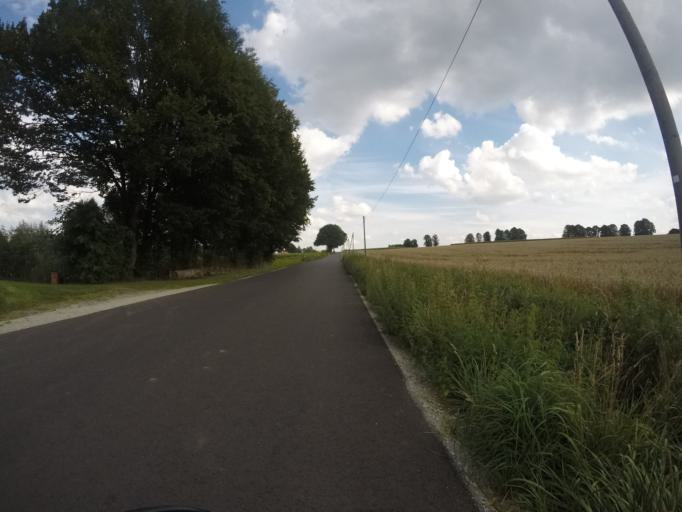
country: DE
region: North Rhine-Westphalia
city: Enger
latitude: 52.0966
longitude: 8.5964
